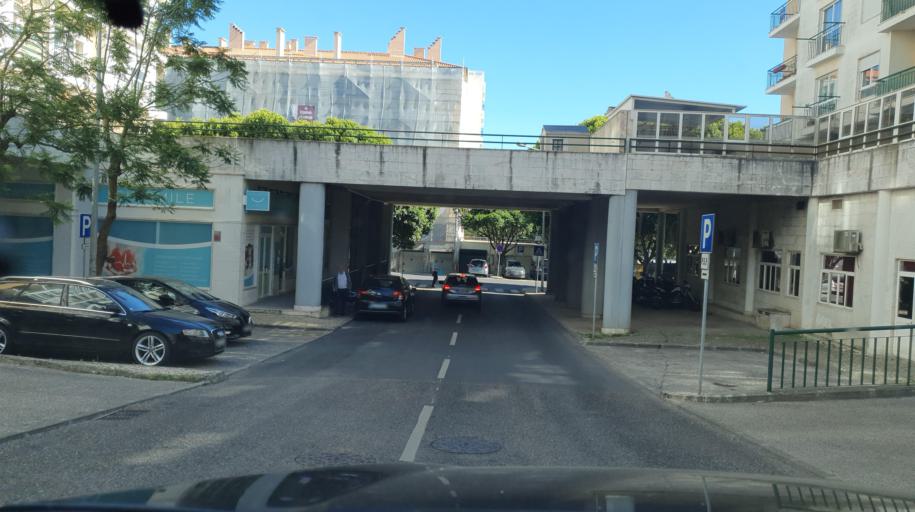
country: PT
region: Lisbon
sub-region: Sintra
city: Cacem
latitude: 38.7586
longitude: -9.2816
